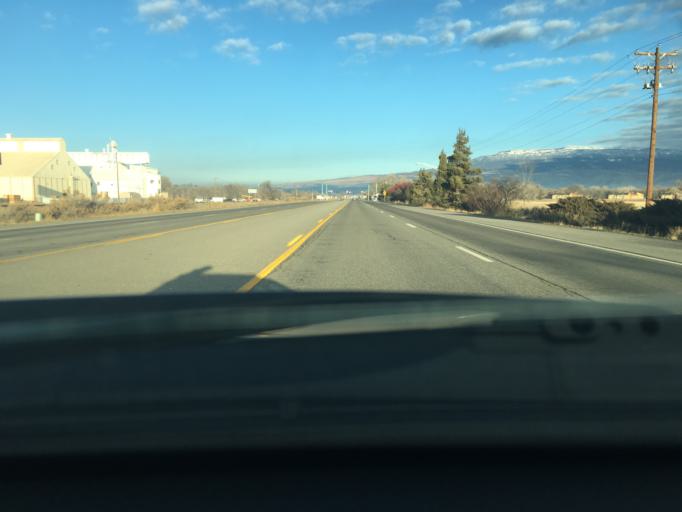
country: US
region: Colorado
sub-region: Delta County
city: Delta
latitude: 38.7223
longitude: -108.0609
